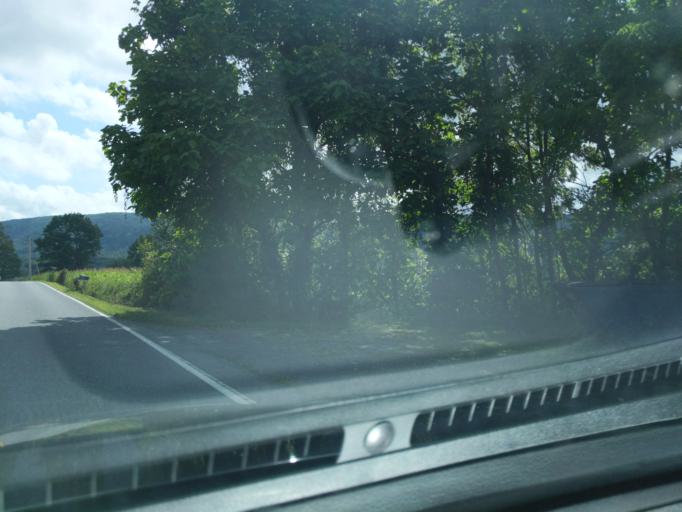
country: US
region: Pennsylvania
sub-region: Blair County
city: Duncansville
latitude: 40.3954
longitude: -78.4230
